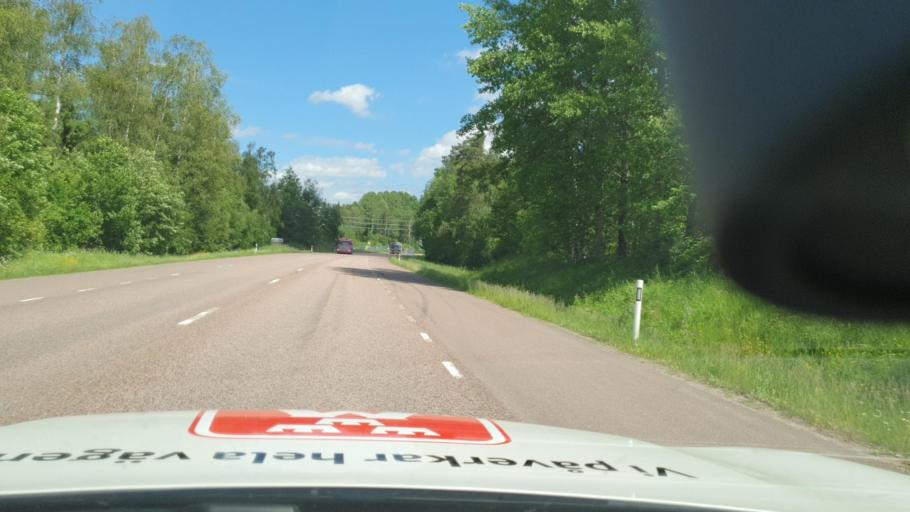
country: SE
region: Vaermland
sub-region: Filipstads Kommun
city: Filipstad
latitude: 59.7111
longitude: 14.1390
